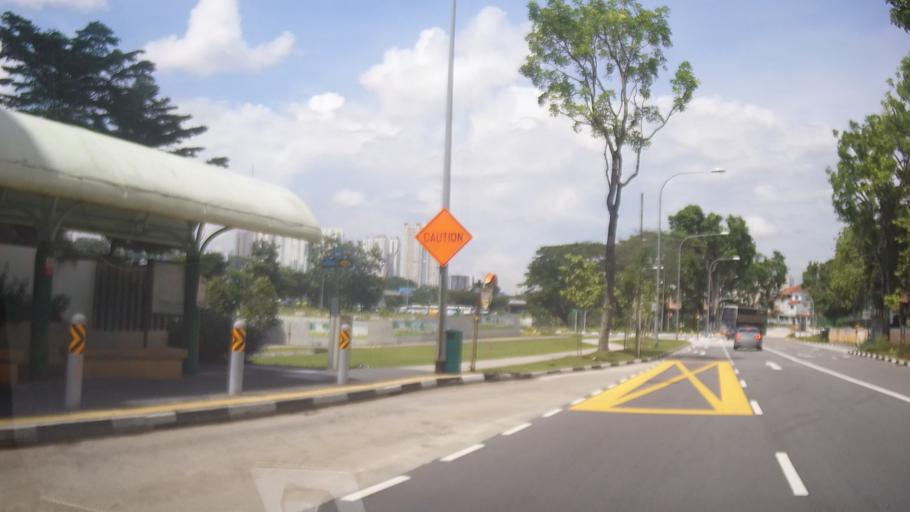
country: MY
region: Johor
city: Johor Bahru
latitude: 1.3954
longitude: 103.7519
